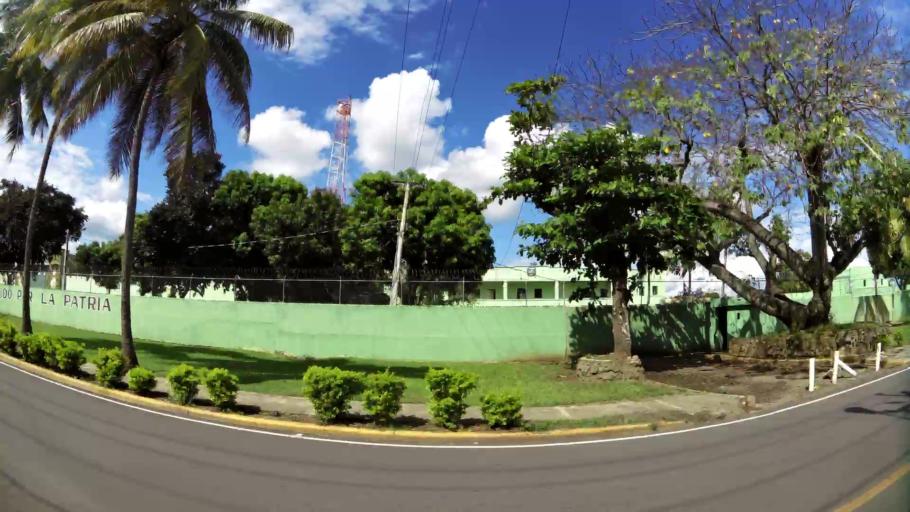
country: DO
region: La Vega
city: Concepcion de La Vega
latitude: 19.2190
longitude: -70.5192
